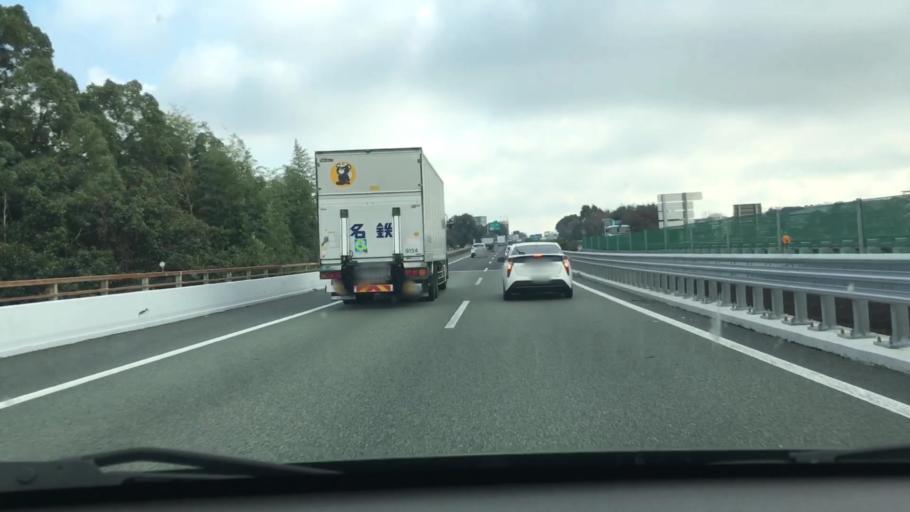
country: JP
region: Kumamoto
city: Kumamoto
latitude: 32.8423
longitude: 130.7705
